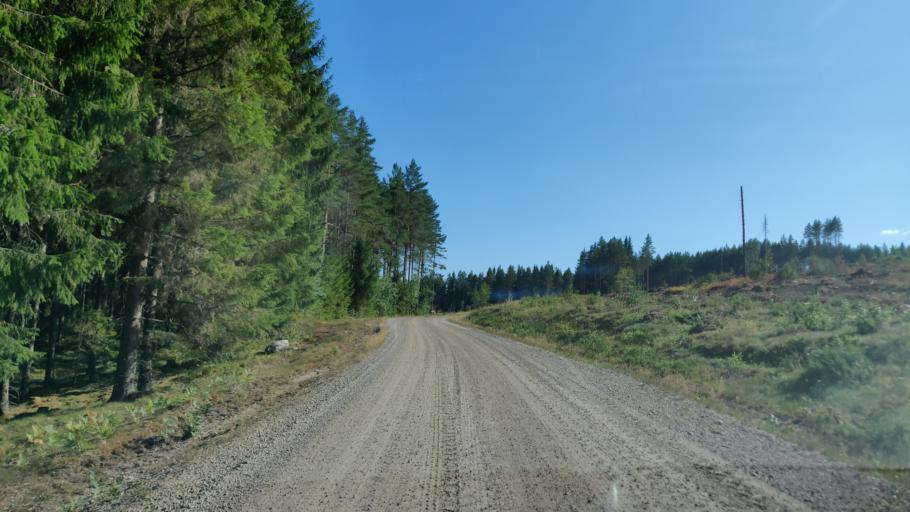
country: SE
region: Vaermland
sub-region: Hagfors Kommun
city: Ekshaerad
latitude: 60.1481
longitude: 13.5168
